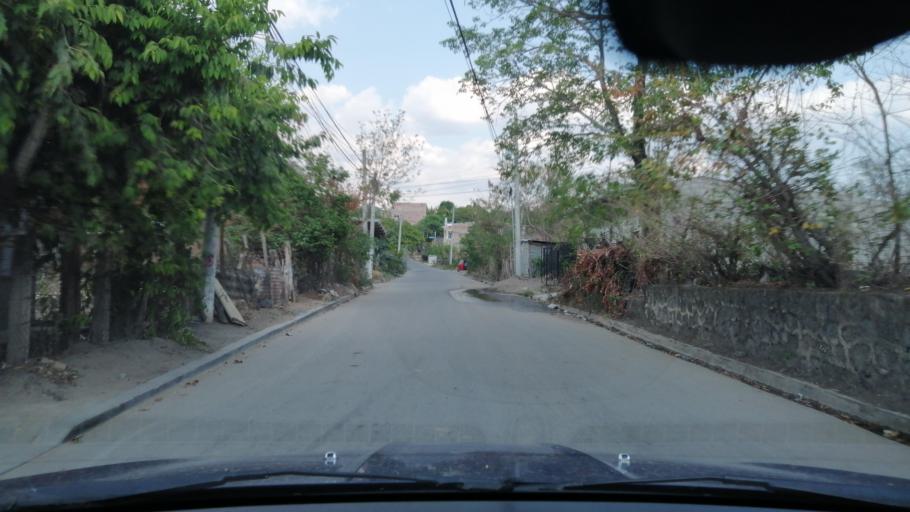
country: SV
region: Santa Ana
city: Metapan
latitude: 14.3297
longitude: -89.4353
